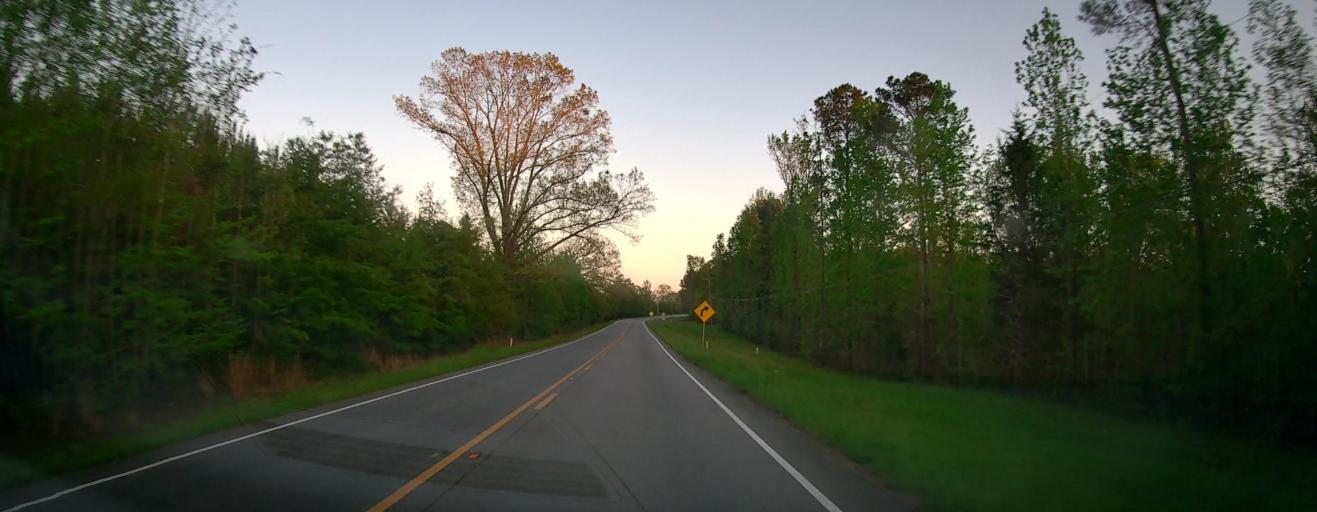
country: US
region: Georgia
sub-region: Marion County
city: Buena Vista
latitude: 32.3511
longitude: -84.5347
